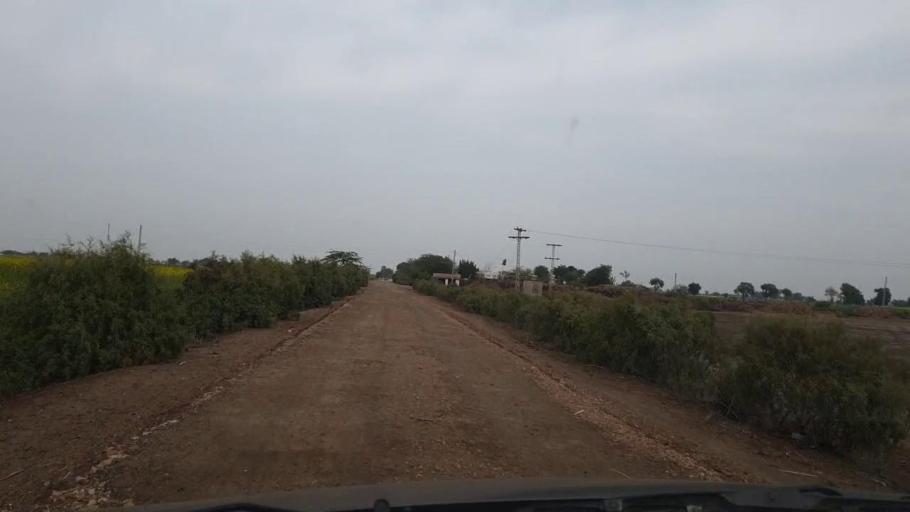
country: PK
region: Sindh
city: Sanghar
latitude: 26.1091
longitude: 68.8963
